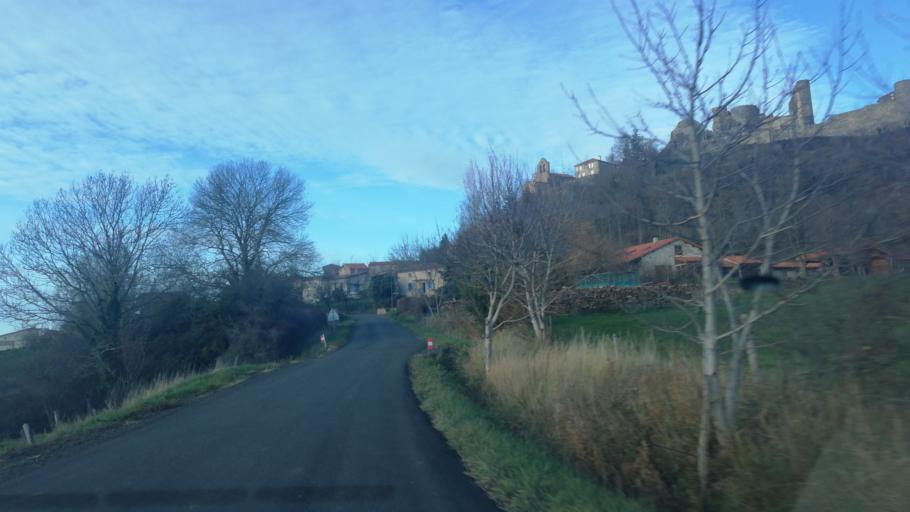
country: FR
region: Auvergne
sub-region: Departement du Puy-de-Dome
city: Billom
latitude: 45.6928
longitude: 3.3597
